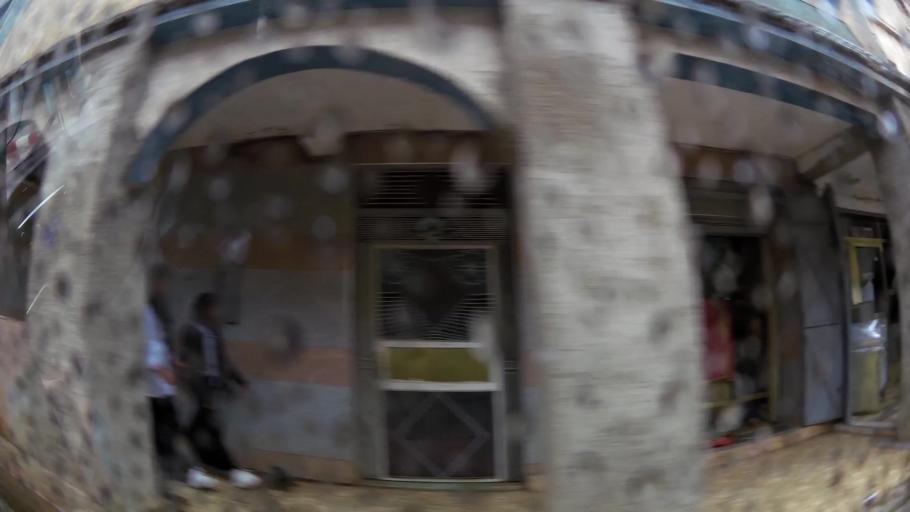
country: MA
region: Oriental
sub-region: Nador
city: Boudinar
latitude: 35.1187
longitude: -3.6408
